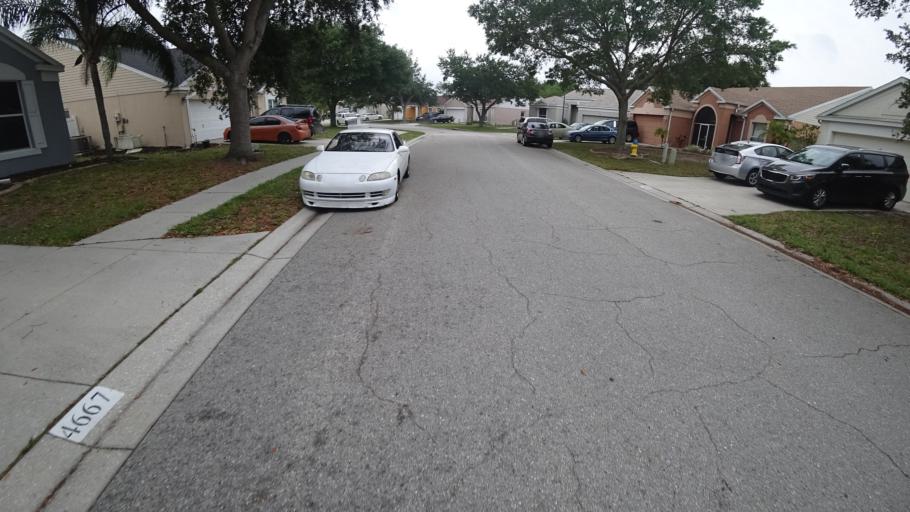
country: US
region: Florida
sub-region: Manatee County
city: Samoset
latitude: 27.4413
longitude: -82.5036
